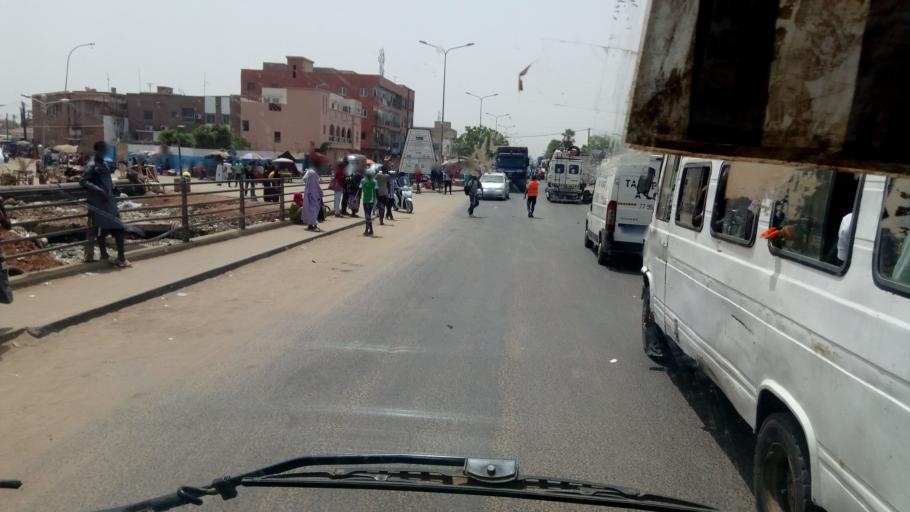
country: SN
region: Dakar
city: Pikine
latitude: 14.7164
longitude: -17.2751
